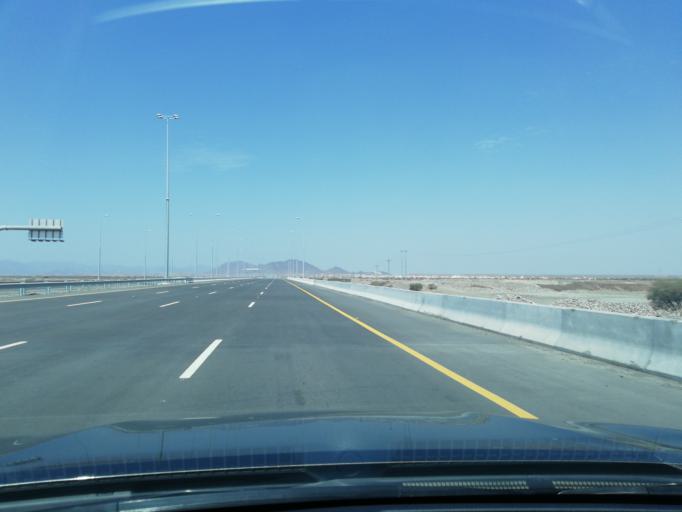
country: OM
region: Al Batinah
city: Rustaq
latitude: 23.5348
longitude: 57.5590
